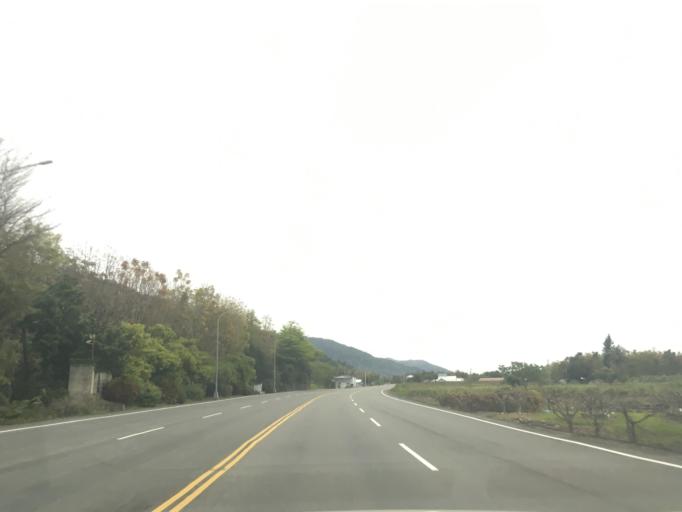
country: TW
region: Taiwan
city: Taitung City
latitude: 22.7306
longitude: 121.0561
